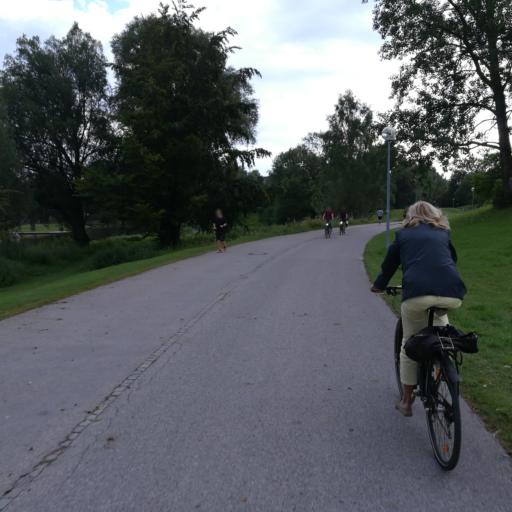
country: DE
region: Bavaria
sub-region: Upper Bavaria
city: Munich
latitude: 48.1728
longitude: 11.5562
